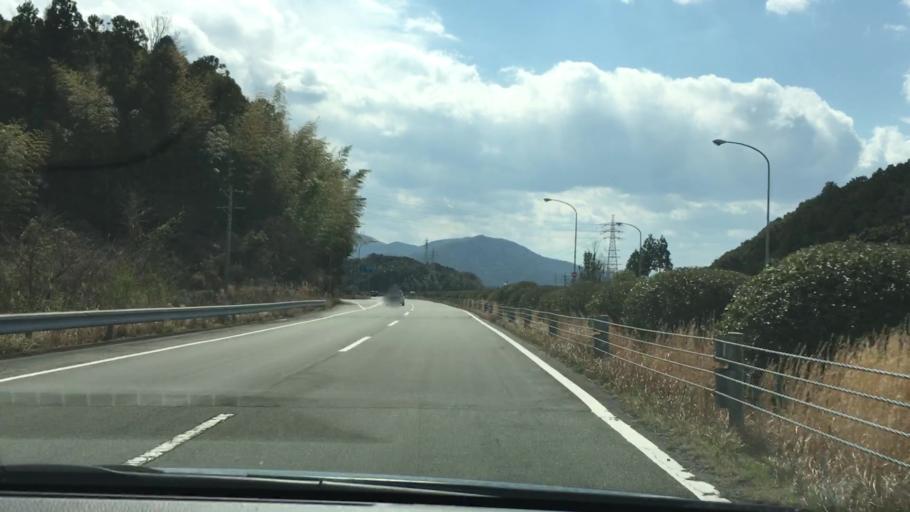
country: JP
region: Mie
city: Ise
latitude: 34.4878
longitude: 136.7576
